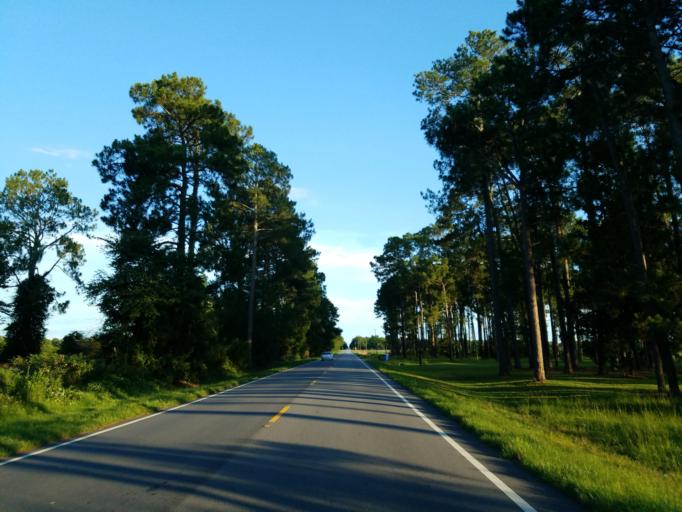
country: US
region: Georgia
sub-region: Tift County
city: Unionville
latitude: 31.3387
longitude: -83.4815
